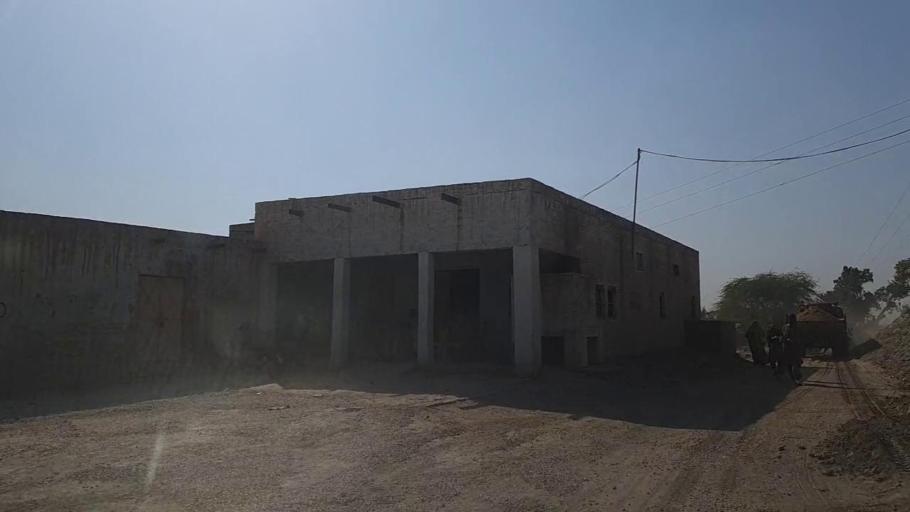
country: PK
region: Sindh
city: Digri
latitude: 25.1001
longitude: 69.1809
